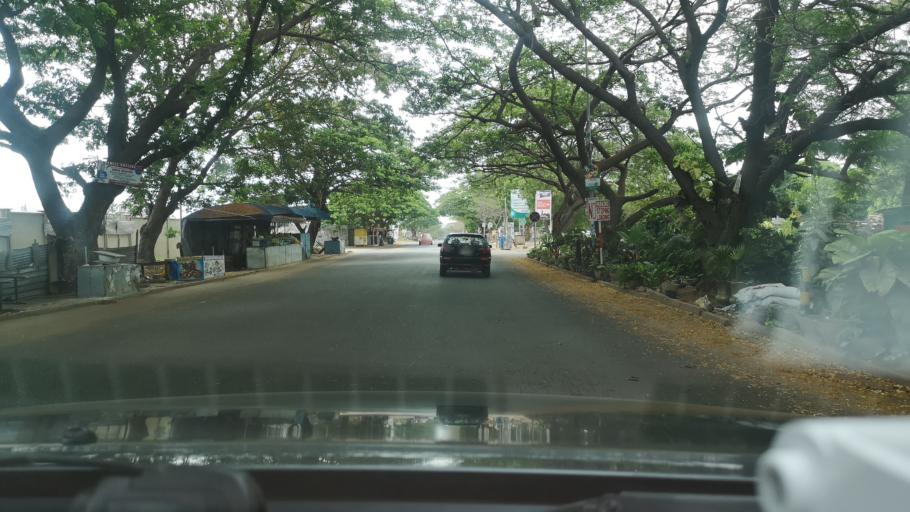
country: GH
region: Greater Accra
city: Nungua
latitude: 5.6237
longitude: -0.0678
